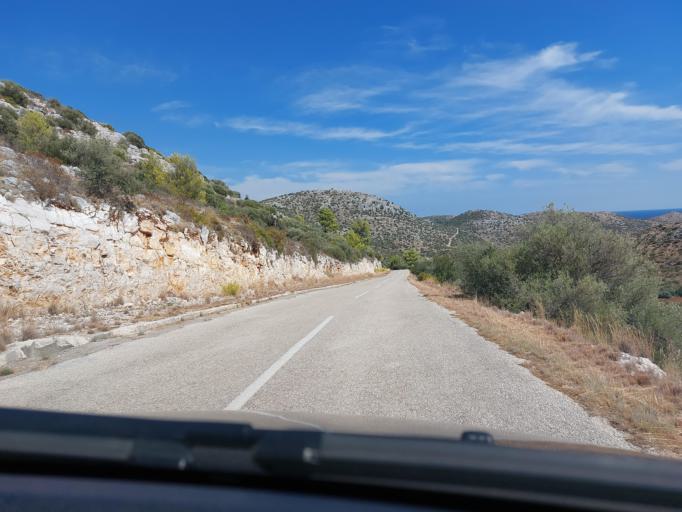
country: HR
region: Dubrovacko-Neretvanska
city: Smokvica
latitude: 42.7442
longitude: 16.8766
